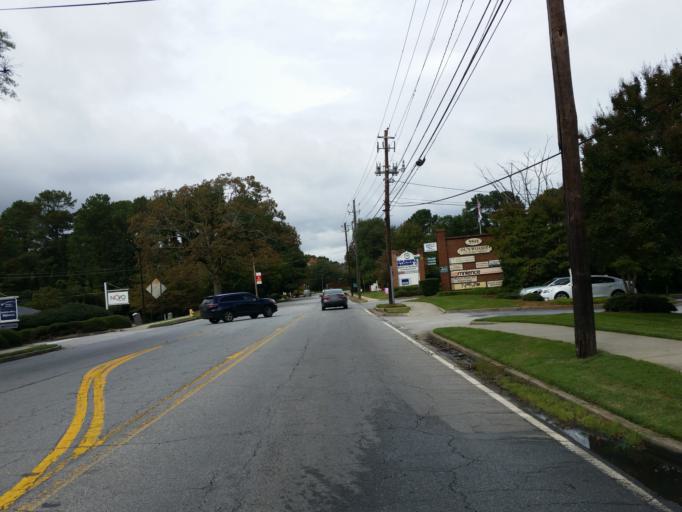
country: US
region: Georgia
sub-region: DeKalb County
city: Dunwoody
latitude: 33.9506
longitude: -84.3364
